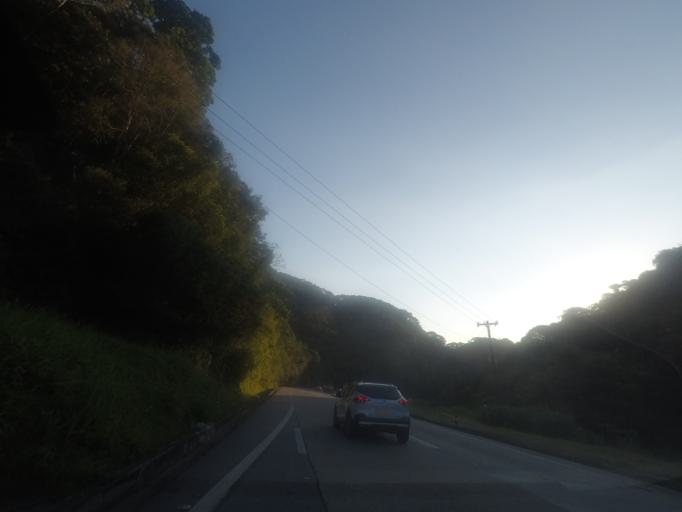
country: BR
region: Rio de Janeiro
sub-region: Petropolis
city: Petropolis
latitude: -22.5208
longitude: -43.2307
